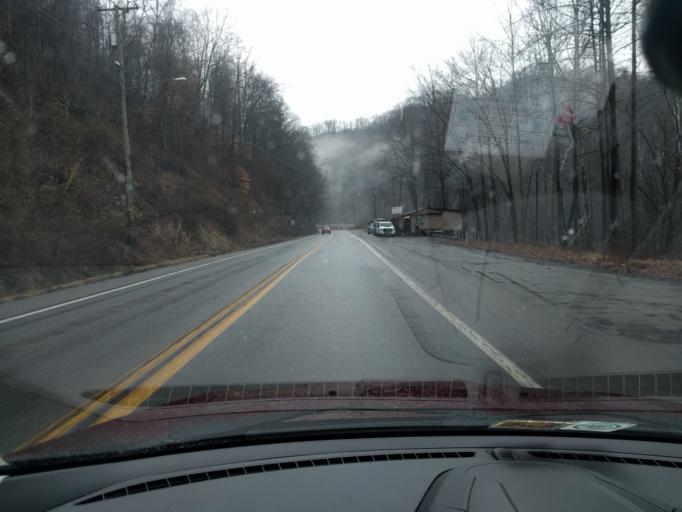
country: US
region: West Virginia
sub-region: McDowell County
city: Welch
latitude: 37.4294
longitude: -81.5604
